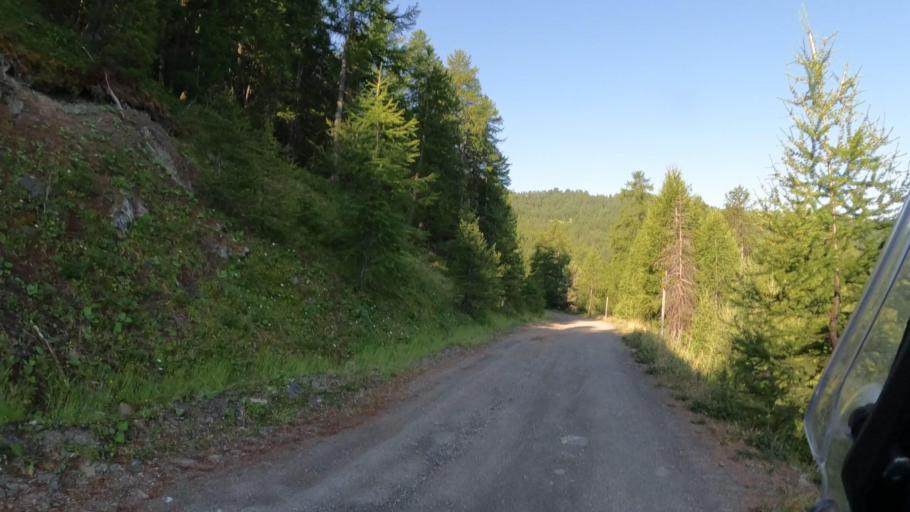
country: FR
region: Provence-Alpes-Cote d'Azur
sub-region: Departement des Hautes-Alpes
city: Guillestre
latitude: 44.6116
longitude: 6.6553
